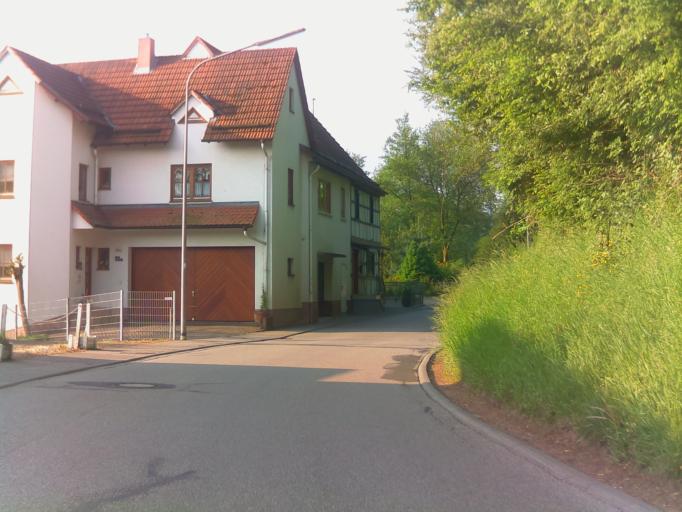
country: DE
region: Hesse
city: Reichelsheim
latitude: 49.6963
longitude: 8.8616
